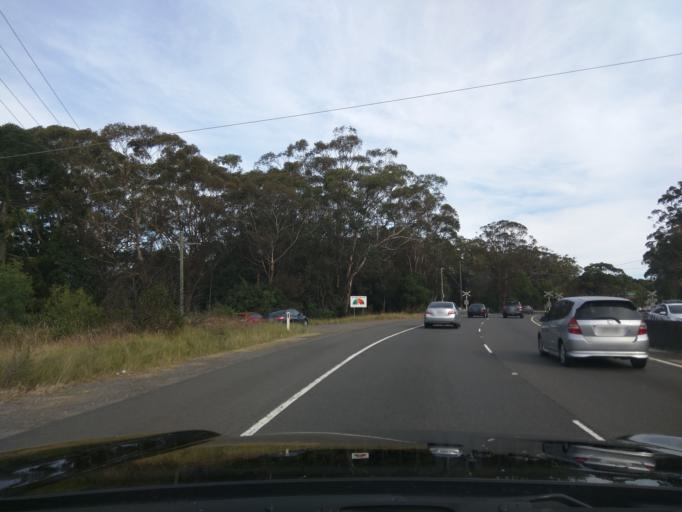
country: AU
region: New South Wales
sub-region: Sutherland Shire
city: Loftus
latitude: -34.0492
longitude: 151.0520
